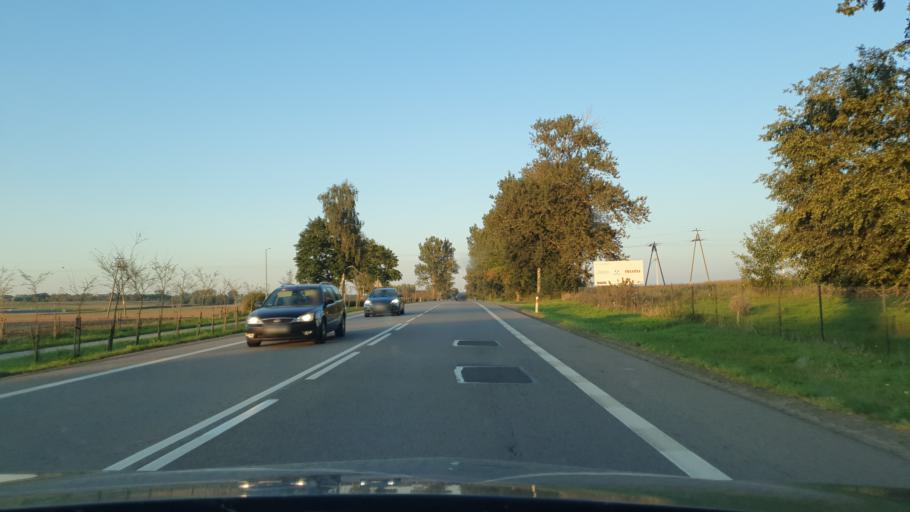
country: PL
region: Pomeranian Voivodeship
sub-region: Powiat slupski
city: Potegowo
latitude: 54.4687
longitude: 17.4720
